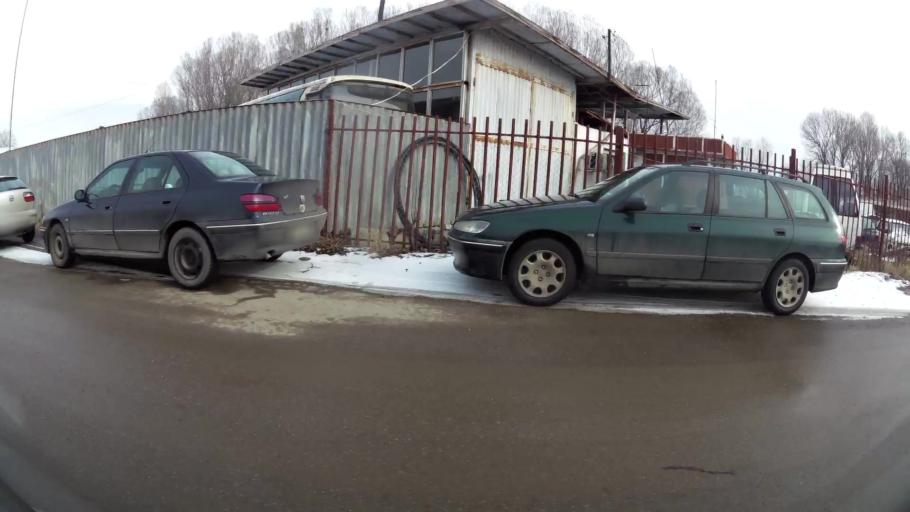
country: BG
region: Sofia-Capital
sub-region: Stolichna Obshtina
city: Sofia
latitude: 42.7151
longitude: 23.4209
